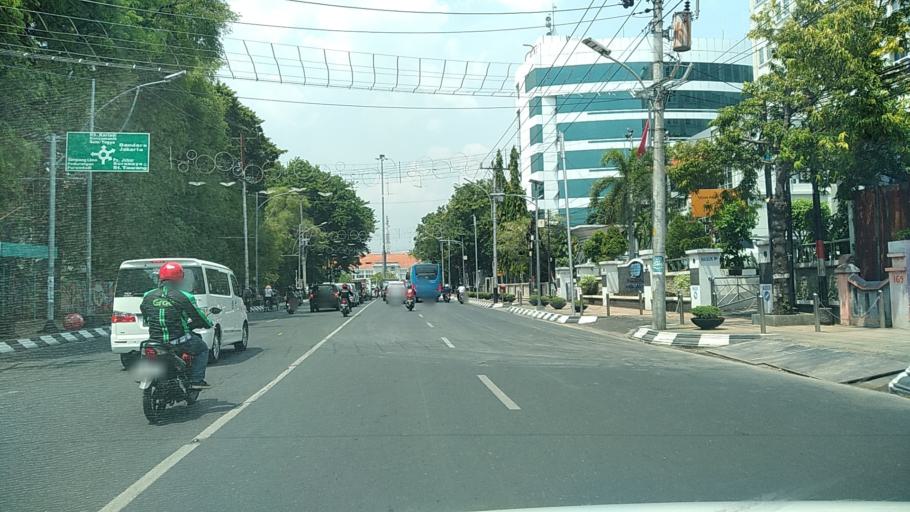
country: ID
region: Central Java
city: Semarang
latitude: -6.9827
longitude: 110.4111
